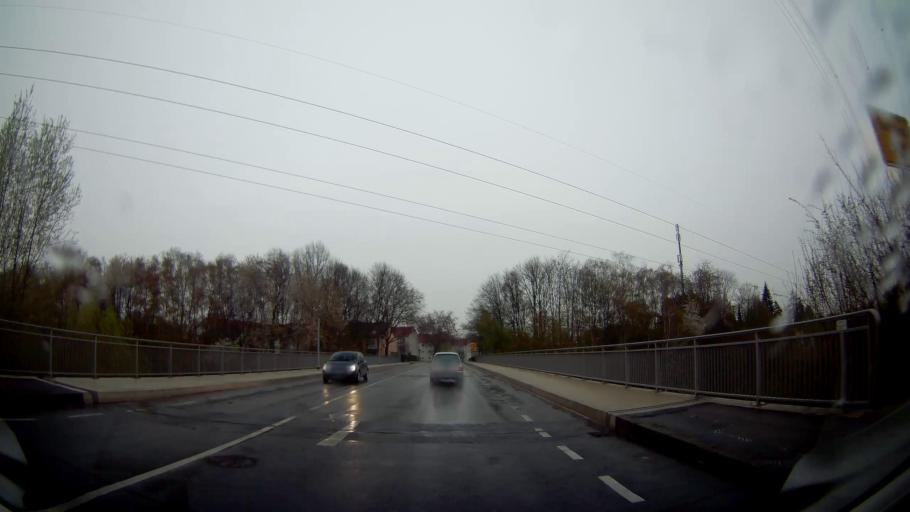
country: DE
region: North Rhine-Westphalia
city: Castrop-Rauxel
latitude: 51.5241
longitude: 7.3778
